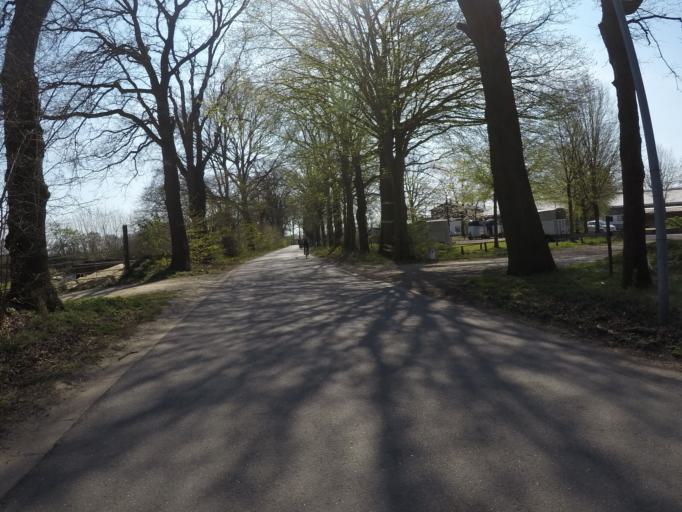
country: DE
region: Schleswig-Holstein
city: Rellingen
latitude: 53.6068
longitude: 9.8011
